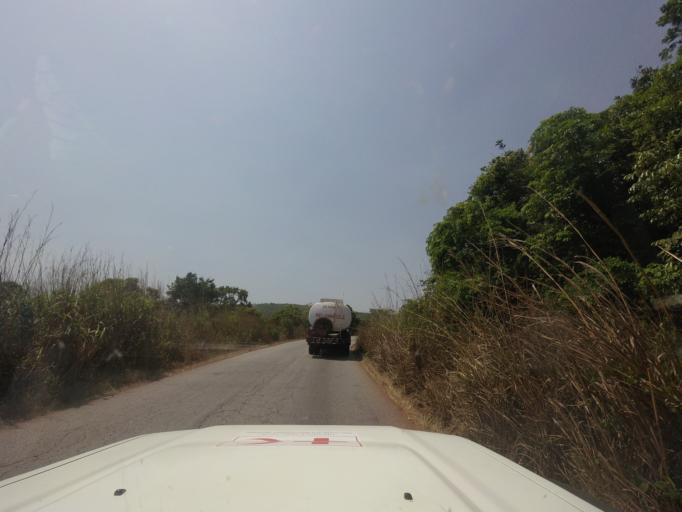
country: GN
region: Kindia
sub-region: Kindia
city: Kindia
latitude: 9.9055
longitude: -12.9967
